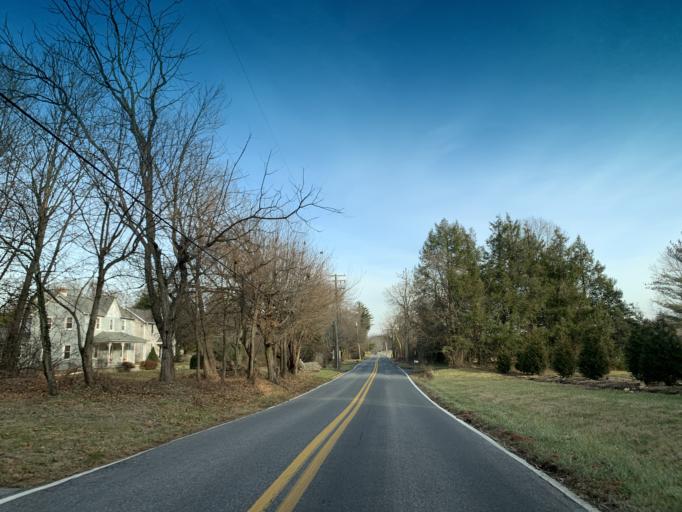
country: US
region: Maryland
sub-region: Baltimore County
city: Hunt Valley
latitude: 39.5574
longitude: -76.5636
